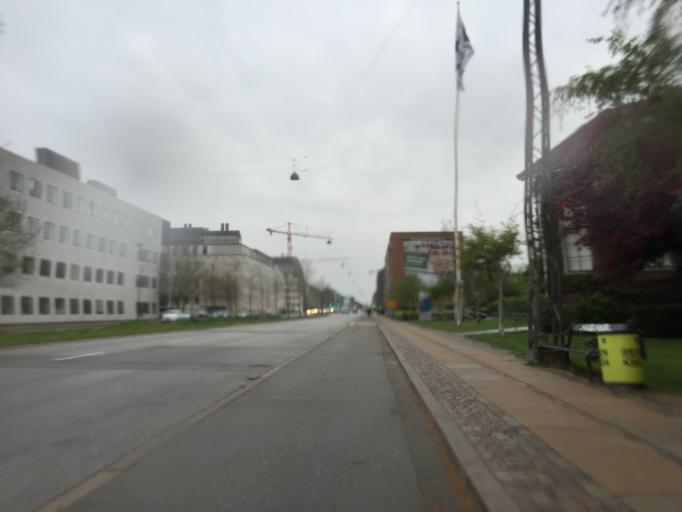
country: DK
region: Capital Region
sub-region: Kobenhavn
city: Copenhagen
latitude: 55.7050
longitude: 12.5607
